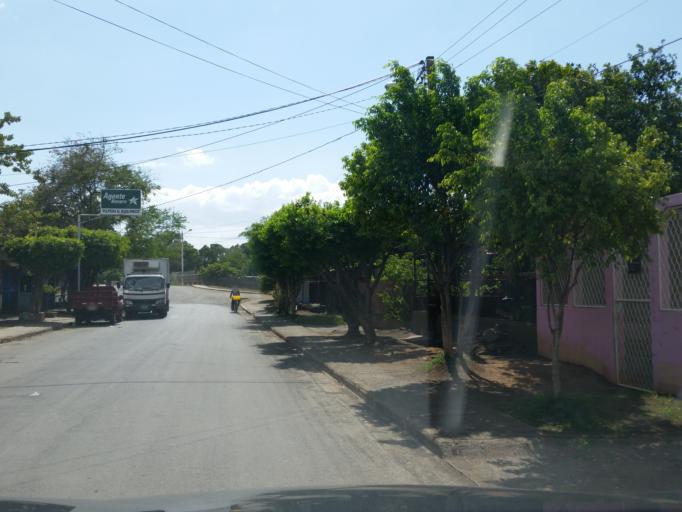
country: NI
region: Managua
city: Managua
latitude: 12.1529
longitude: -86.2083
